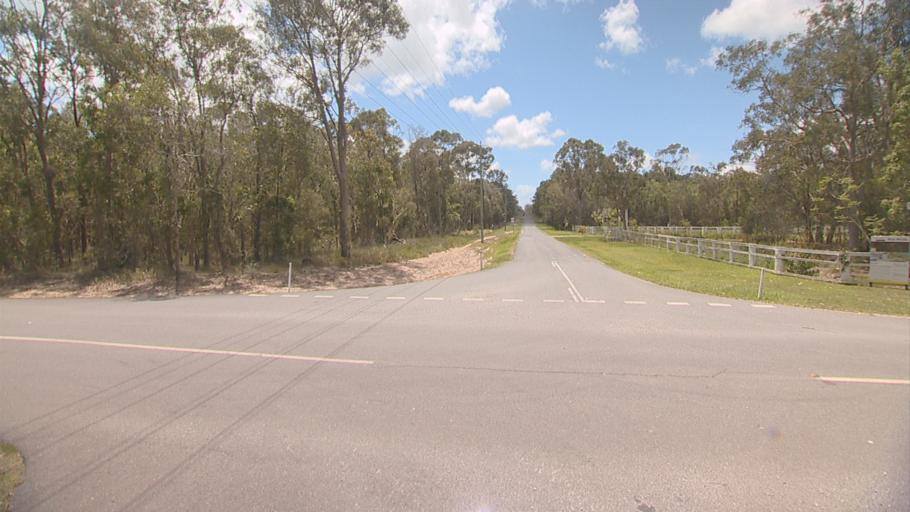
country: AU
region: Queensland
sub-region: Gold Coast
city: Yatala
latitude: -27.6679
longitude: 153.2402
